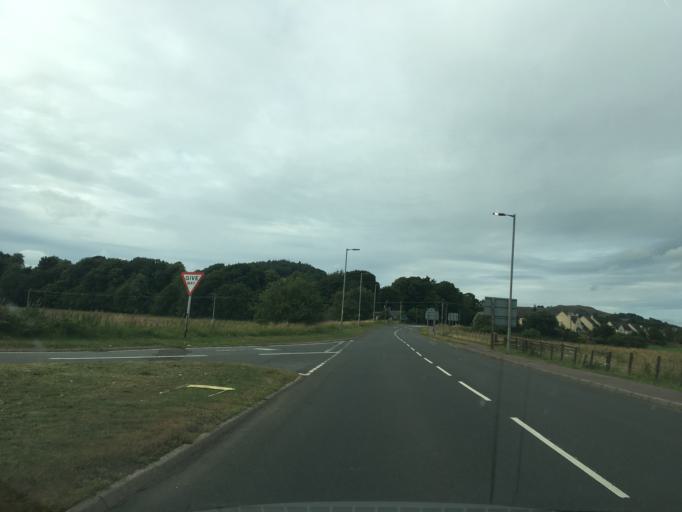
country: GB
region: Scotland
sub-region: South Lanarkshire
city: Biggar
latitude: 55.6144
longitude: -3.5384
